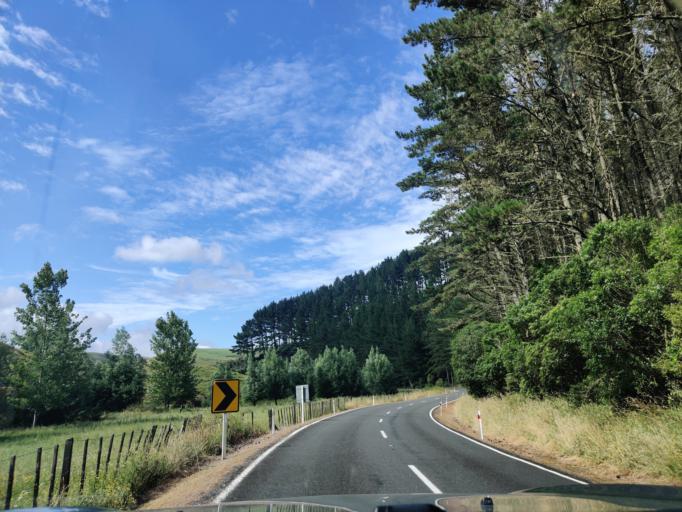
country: NZ
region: Waikato
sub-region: Otorohanga District
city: Otorohanga
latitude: -38.0982
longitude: 175.1311
